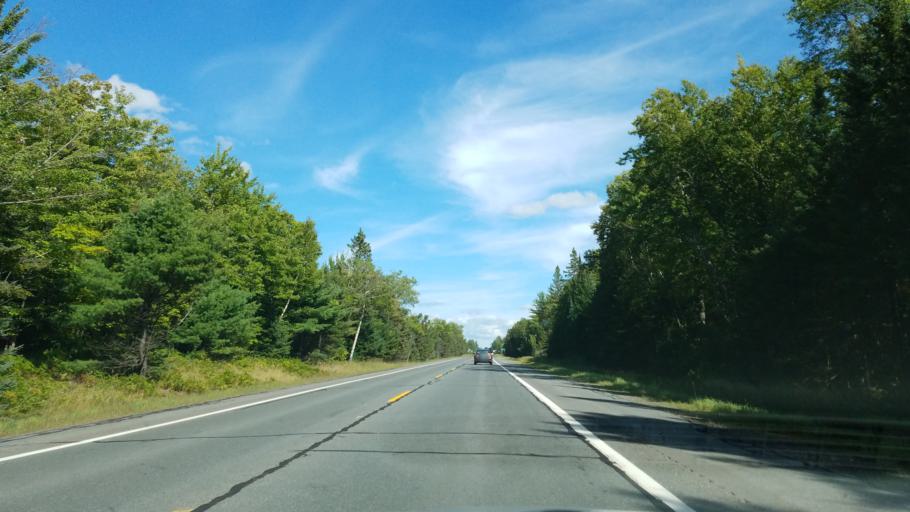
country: US
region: Michigan
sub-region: Baraga County
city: L'Anse
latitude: 46.5788
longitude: -88.4034
